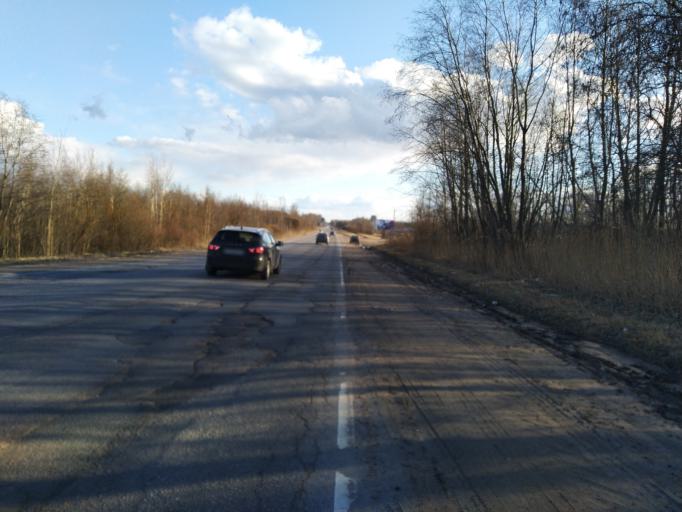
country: RU
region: Leningrad
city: Novoye Devyatkino
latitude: 60.1041
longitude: 30.4995
